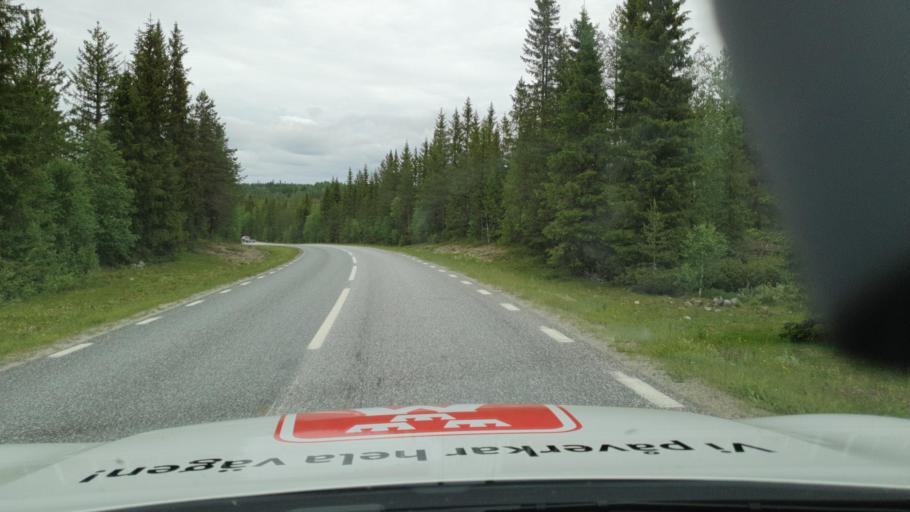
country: SE
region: Vaesterbotten
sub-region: Asele Kommun
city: Insjon
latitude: 64.3483
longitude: 17.8964
